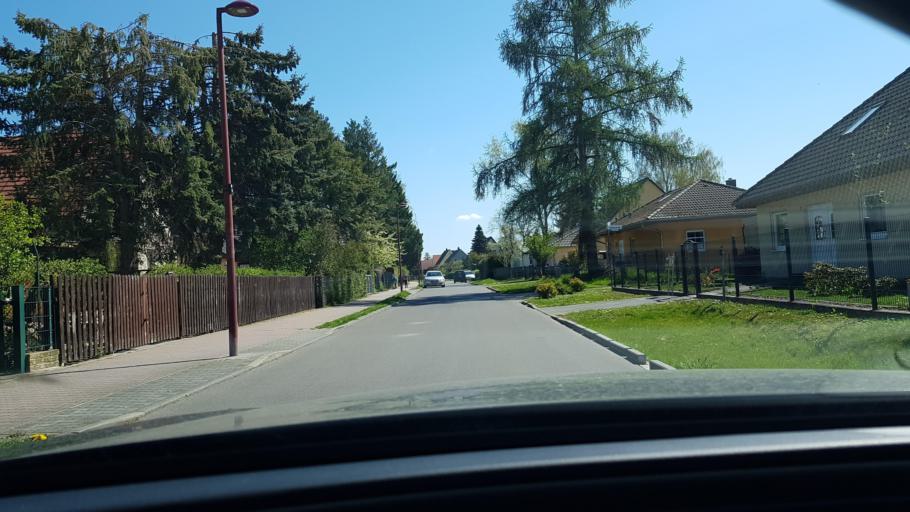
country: DE
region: Brandenburg
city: Rangsdorf
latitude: 52.3419
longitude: 13.4041
